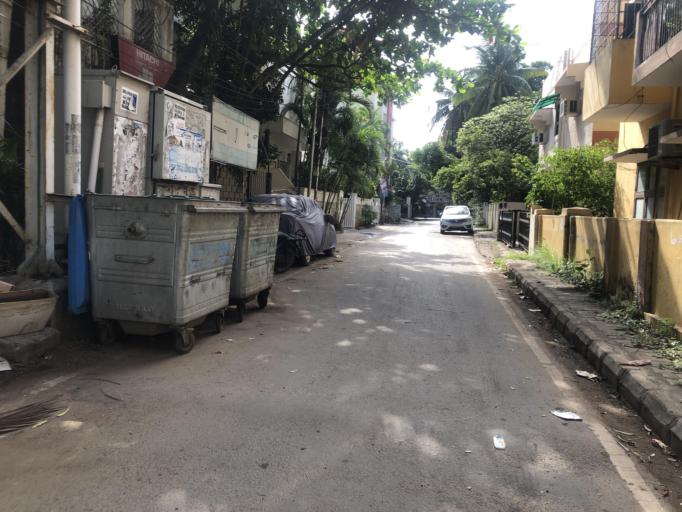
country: IN
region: Tamil Nadu
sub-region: Chennai
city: Gandhi Nagar
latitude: 13.0355
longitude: 80.2589
